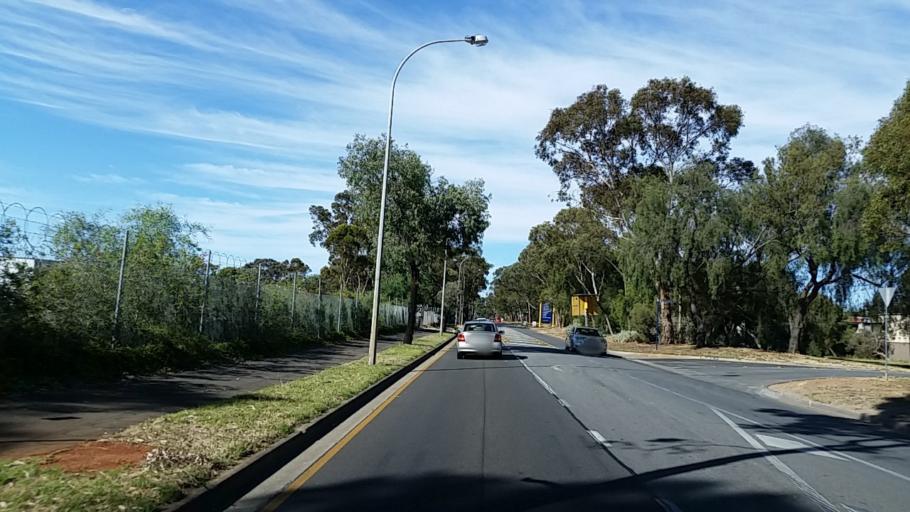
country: AU
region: South Australia
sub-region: Salisbury
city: Salisbury
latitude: -34.7819
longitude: 138.6397
